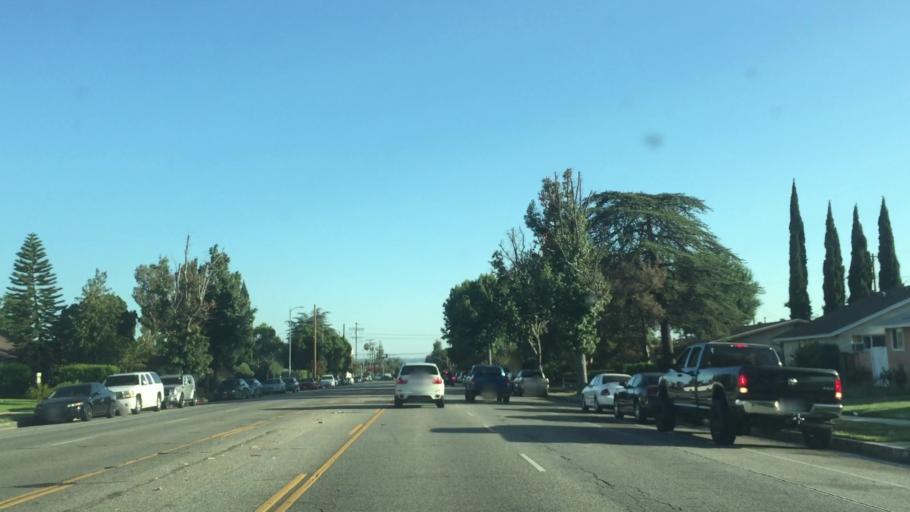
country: US
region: California
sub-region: Los Angeles County
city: Northridge
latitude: 34.2381
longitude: -118.4851
